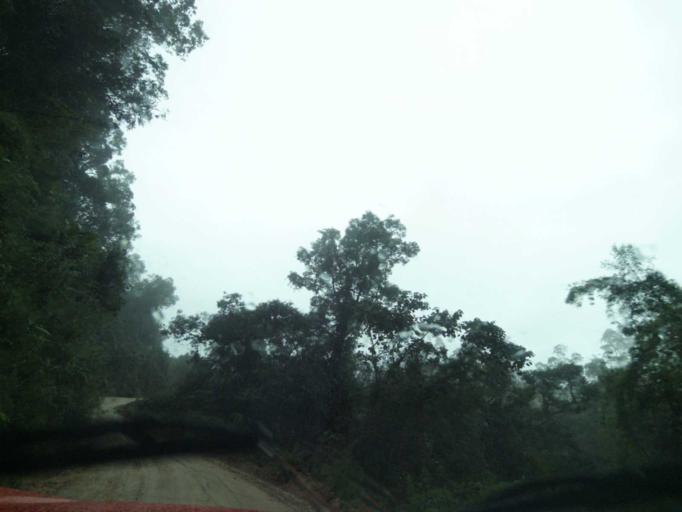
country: BR
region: Santa Catarina
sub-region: Anitapolis
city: Anitapolis
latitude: -27.8925
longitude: -49.1920
